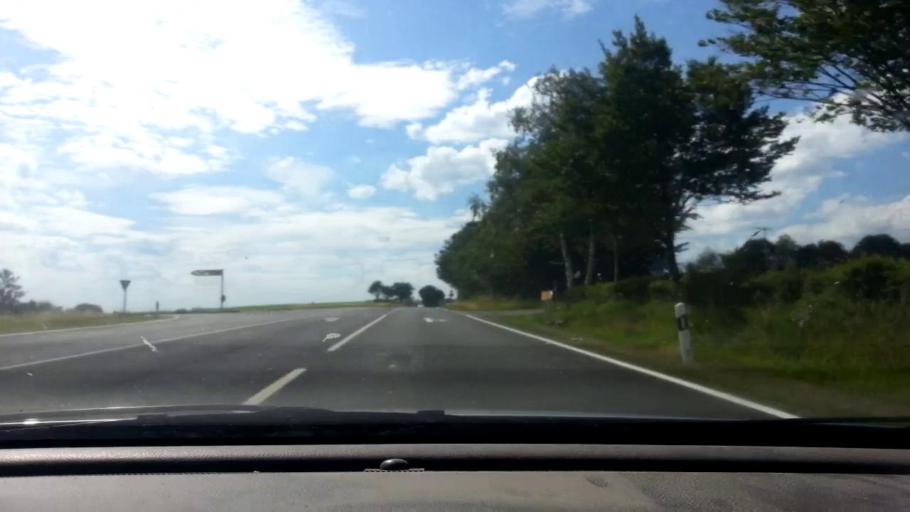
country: DE
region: Bavaria
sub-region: Upper Palatinate
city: Erbendorf
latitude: 49.8512
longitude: 11.9840
